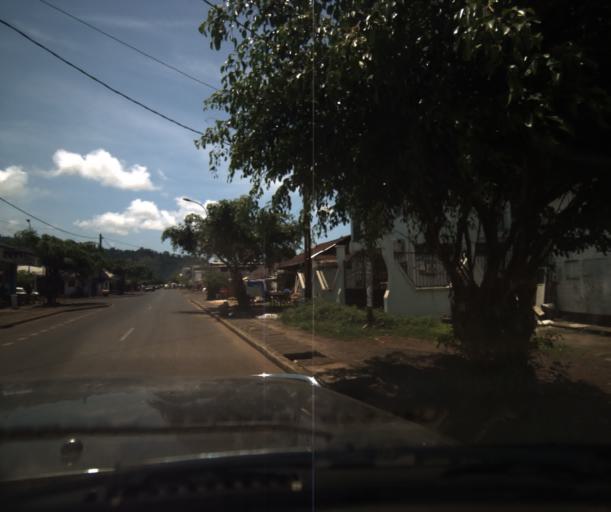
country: CM
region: South-West Province
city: Limbe
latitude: 4.0089
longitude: 9.2072
